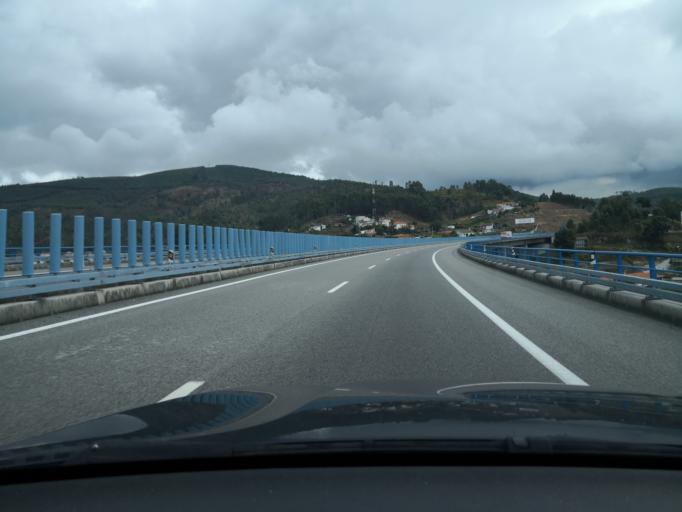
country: PT
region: Porto
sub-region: Pacos de Ferreira
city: Freamunde
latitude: 41.2947
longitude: -8.3087
